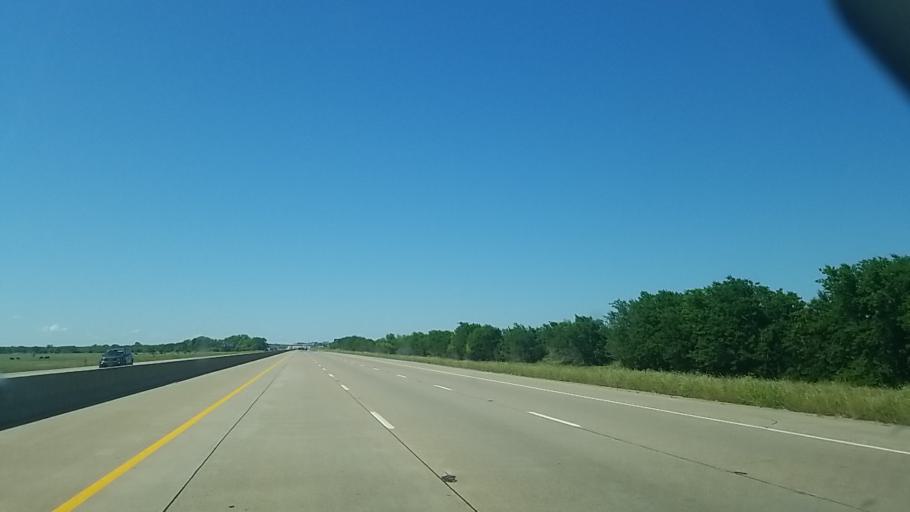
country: US
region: Texas
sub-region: Navarro County
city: Corsicana
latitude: 32.1696
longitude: -96.4700
